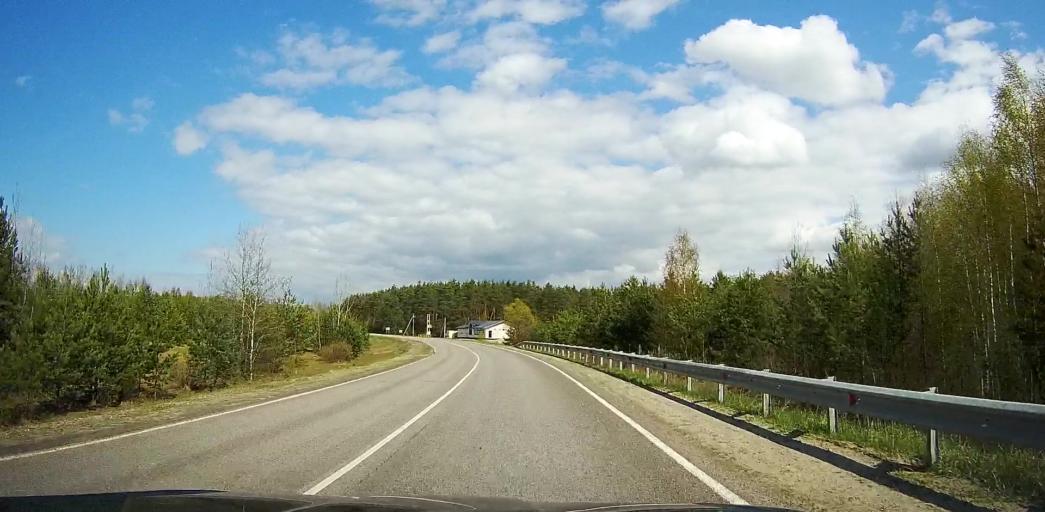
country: RU
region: Moskovskaya
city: Davydovo
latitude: 55.5480
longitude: 38.8159
